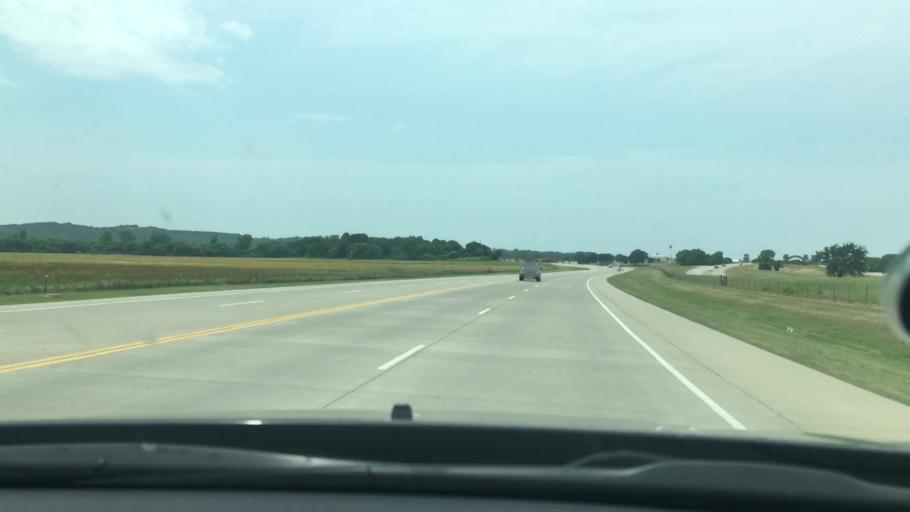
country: US
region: Texas
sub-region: Cooke County
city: Gainesville
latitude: 33.7444
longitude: -97.1384
